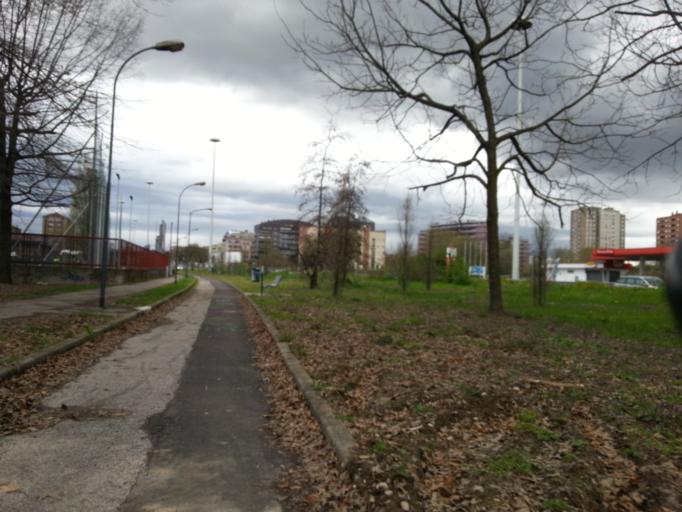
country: IT
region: Lombardy
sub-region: Citta metropolitana di Milano
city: Bresso
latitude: 45.5194
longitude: 9.1767
